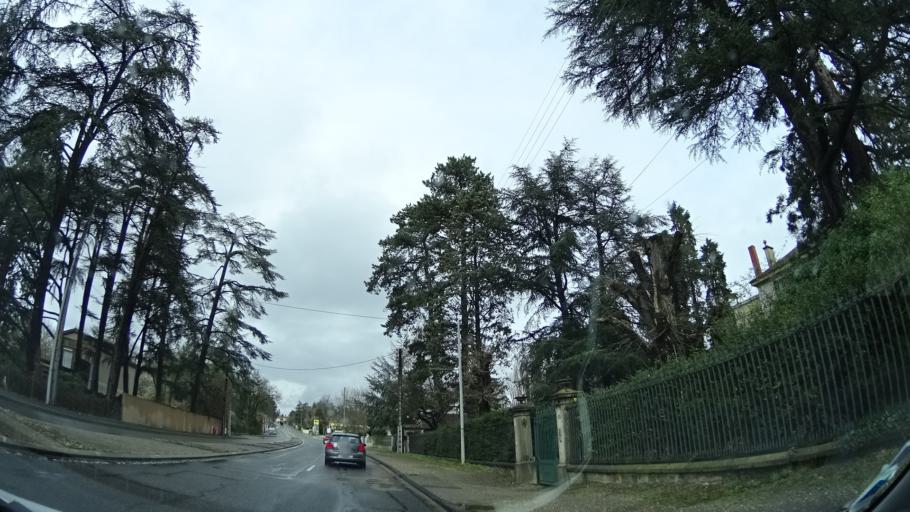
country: FR
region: Rhone-Alpes
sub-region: Departement du Rhone
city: Charbonnieres-les-Bains
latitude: 45.7826
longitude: 4.7502
